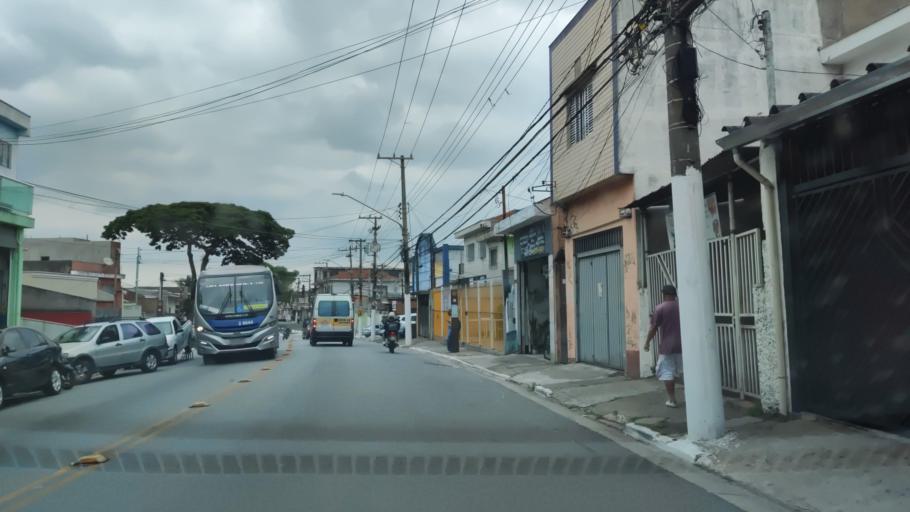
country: BR
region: Sao Paulo
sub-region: Sao Paulo
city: Sao Paulo
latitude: -23.4782
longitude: -46.6508
